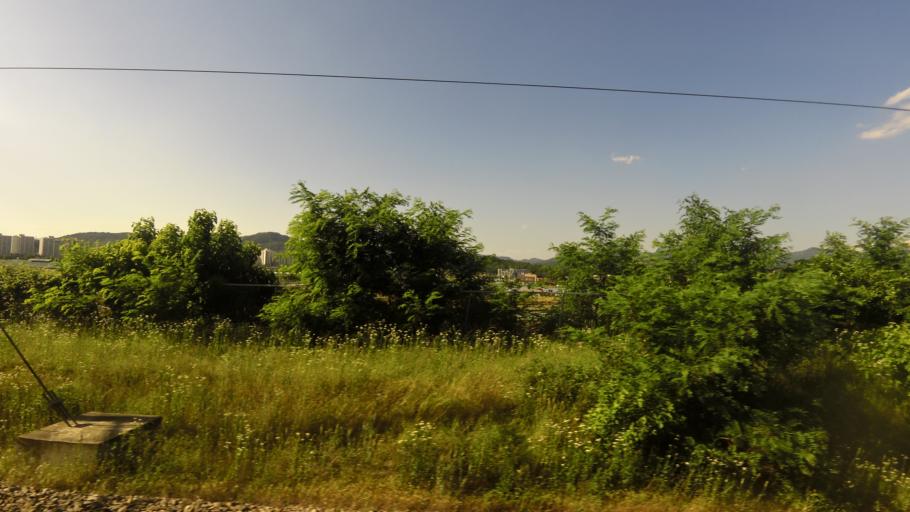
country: KR
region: Gyeongsangbuk-do
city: Waegwan
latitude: 35.9789
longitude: 128.4201
